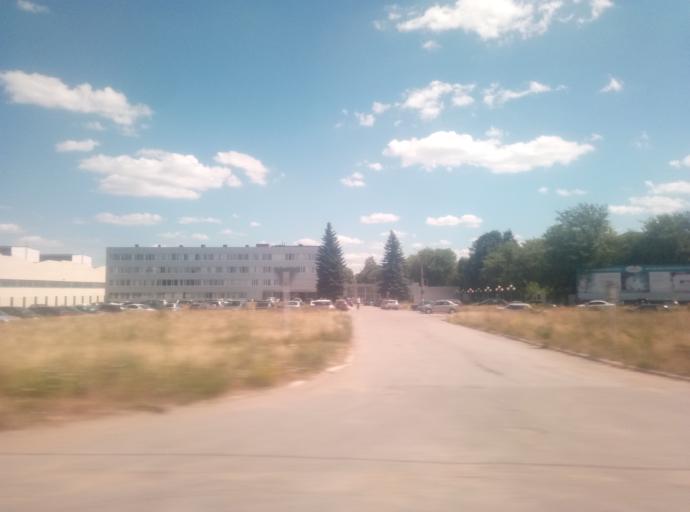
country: RU
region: Tula
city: Kireyevsk
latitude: 53.9572
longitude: 37.9383
